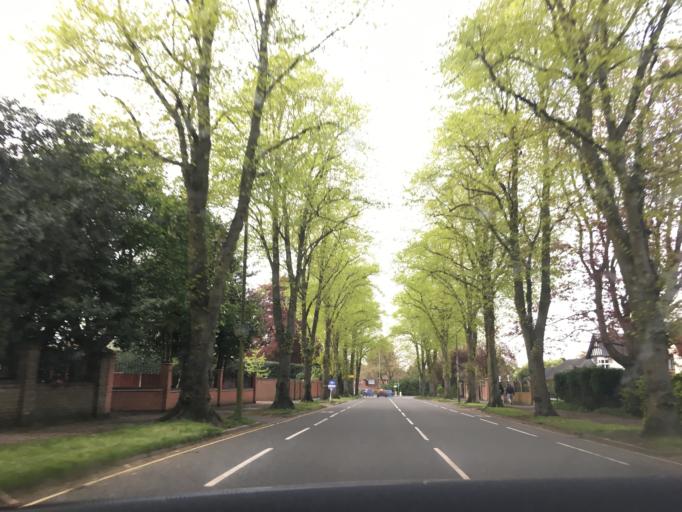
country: GB
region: England
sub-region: Leicestershire
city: Oadby
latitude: 52.6316
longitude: -1.0638
